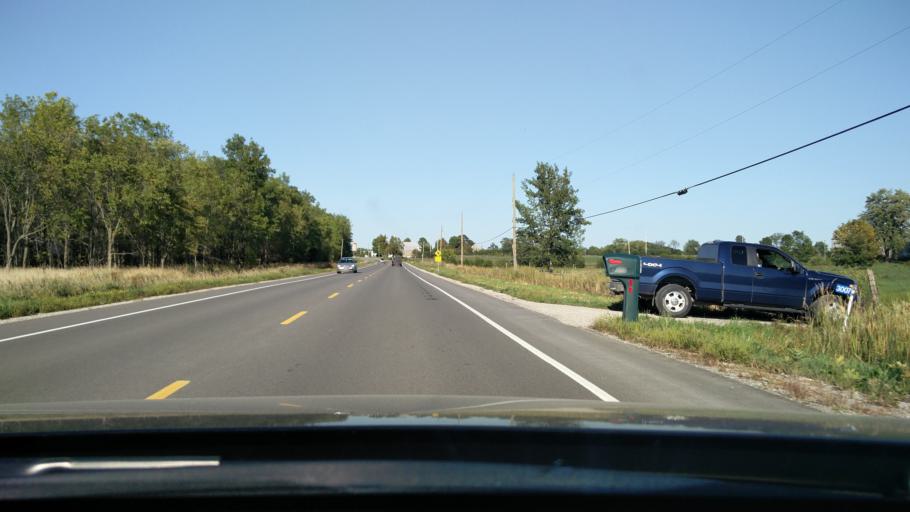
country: CA
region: Ontario
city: Perth
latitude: 44.9470
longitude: -76.1764
